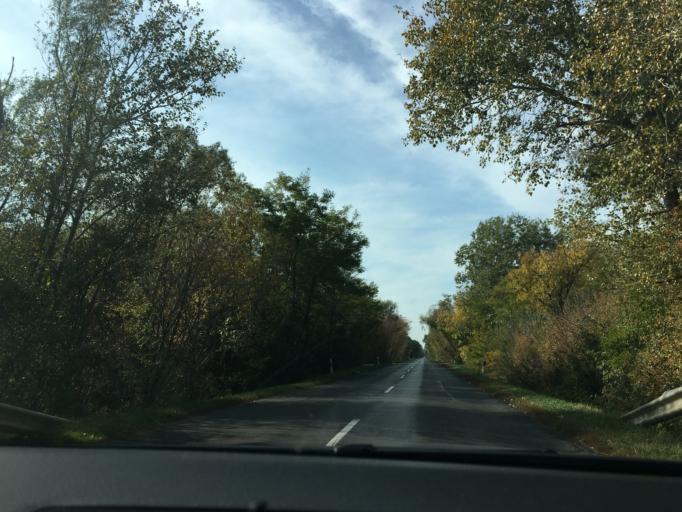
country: HU
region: Hajdu-Bihar
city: Hajdusamson
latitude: 47.5253
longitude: 21.7548
